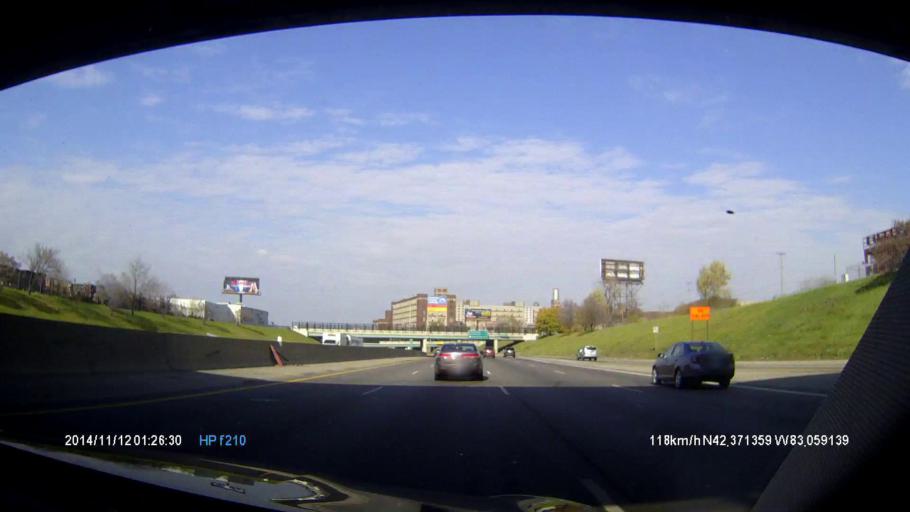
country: US
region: Michigan
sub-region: Wayne County
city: Hamtramck
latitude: 42.3720
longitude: -83.0593
